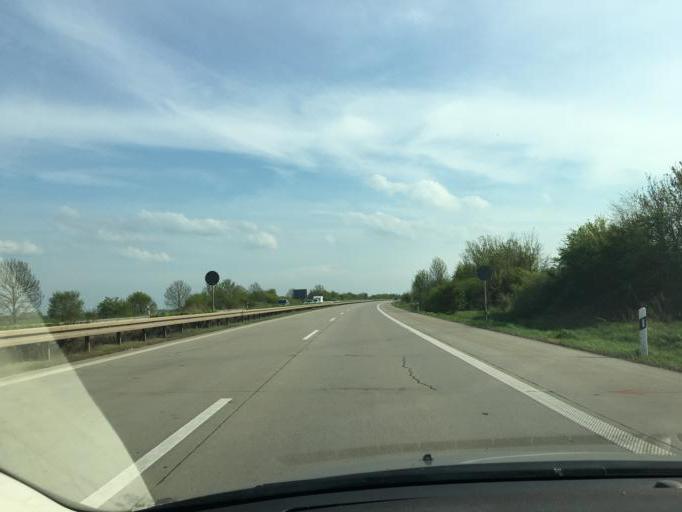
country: DE
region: Saxony-Anhalt
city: Dahlenwarsleben
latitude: 52.1996
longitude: 11.5494
